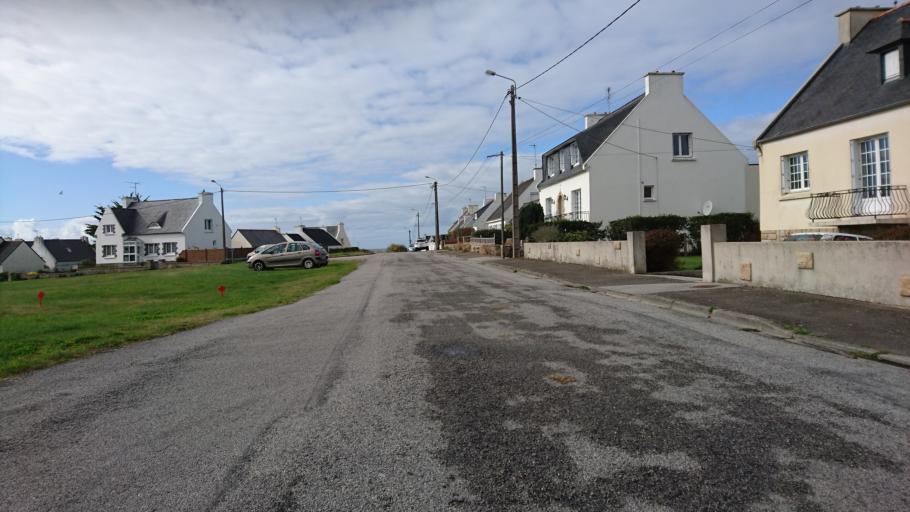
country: FR
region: Brittany
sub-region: Departement du Finistere
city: Lampaul-Plouarzel
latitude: 48.4470
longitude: -4.7693
